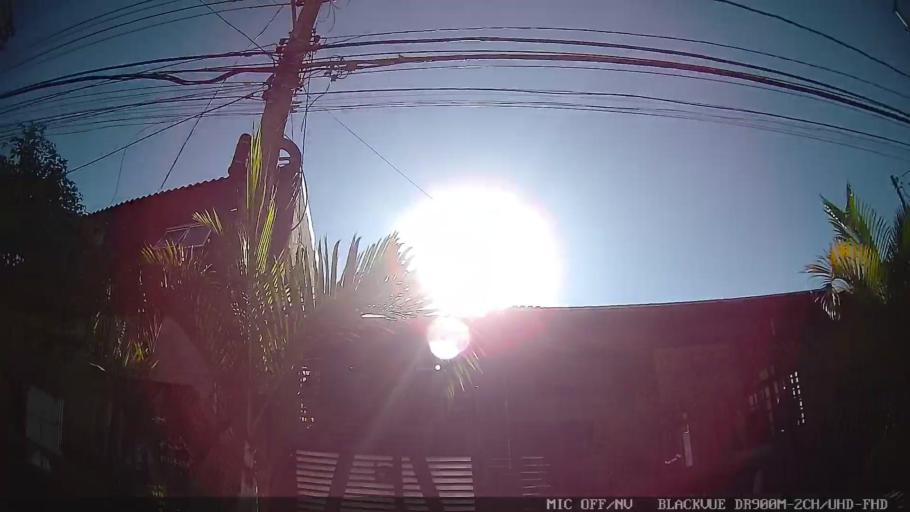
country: BR
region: Sao Paulo
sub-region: Guarulhos
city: Guarulhos
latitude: -23.5369
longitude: -46.5199
